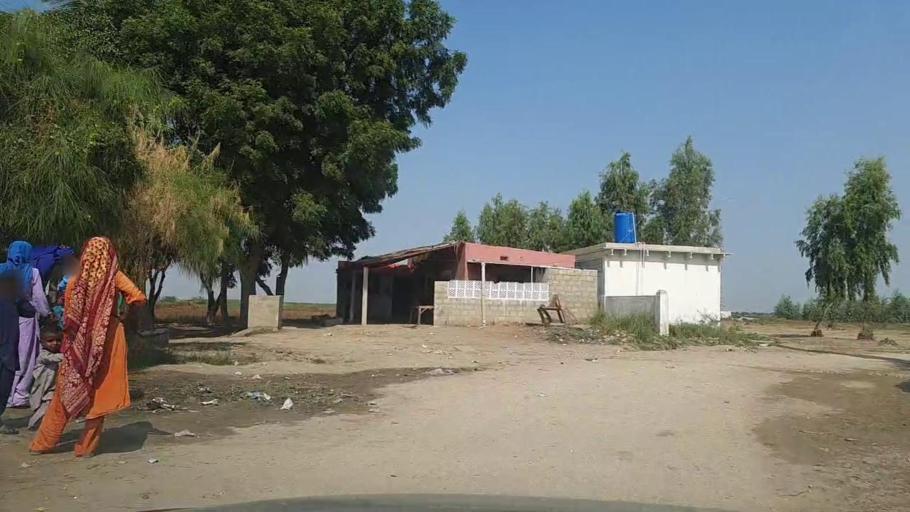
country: PK
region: Sindh
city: Thatta
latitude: 24.6231
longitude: 67.9649
